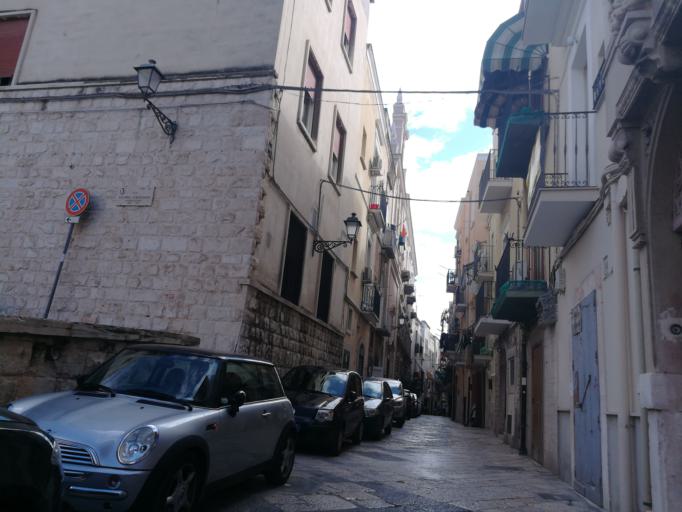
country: IT
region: Apulia
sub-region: Provincia di Bari
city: Bari
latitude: 41.1268
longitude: 16.8693
